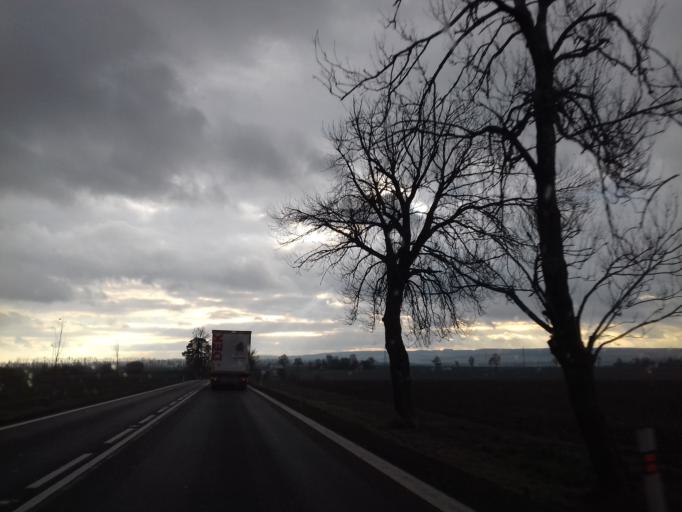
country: CZ
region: Pardubicky
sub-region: Okres Svitavy
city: Svitavy
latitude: 49.7649
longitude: 16.5137
